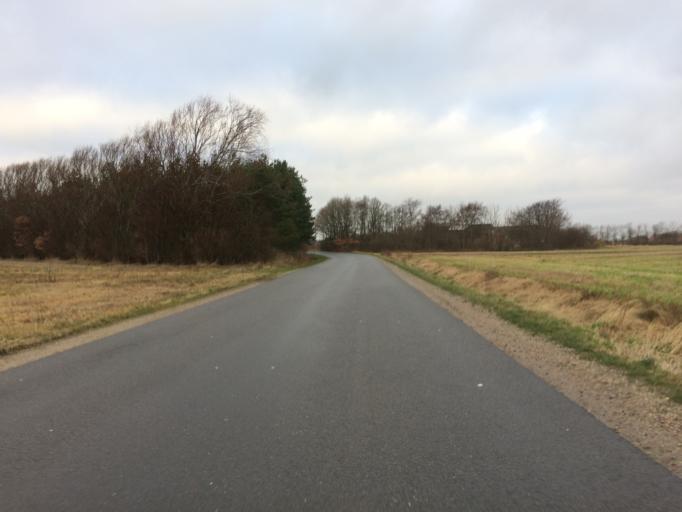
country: DK
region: Central Jutland
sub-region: Holstebro Kommune
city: Ulfborg
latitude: 56.2715
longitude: 8.2815
